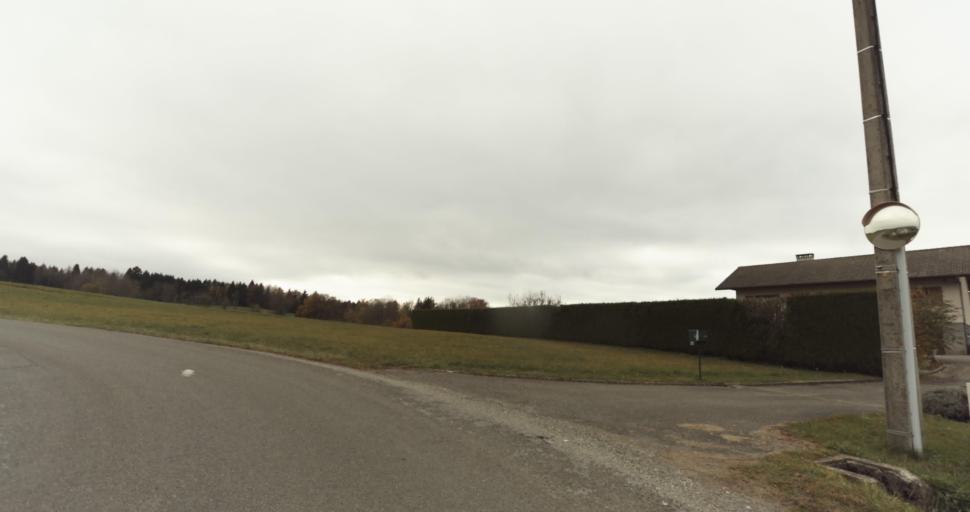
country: FR
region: Rhone-Alpes
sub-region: Departement de la Haute-Savoie
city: Groisy
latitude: 45.9907
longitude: 6.2021
